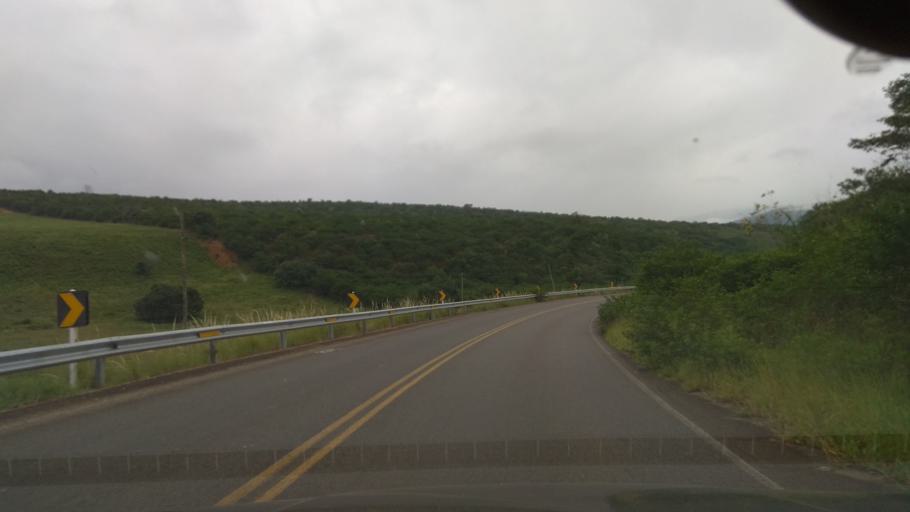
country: BR
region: Bahia
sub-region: Santa Ines
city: Santa Ines
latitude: -13.2530
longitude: -39.7826
